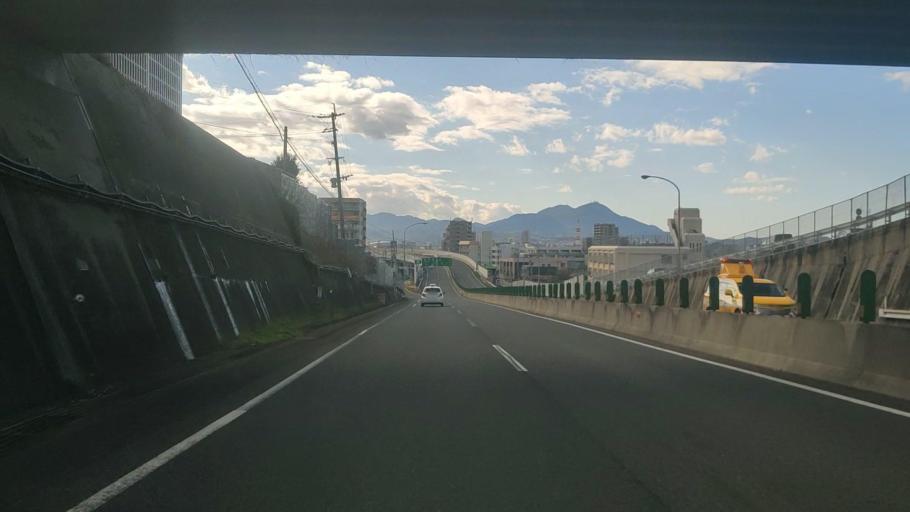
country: JP
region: Yamaguchi
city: Shimonoseki
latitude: 33.8854
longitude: 130.9097
